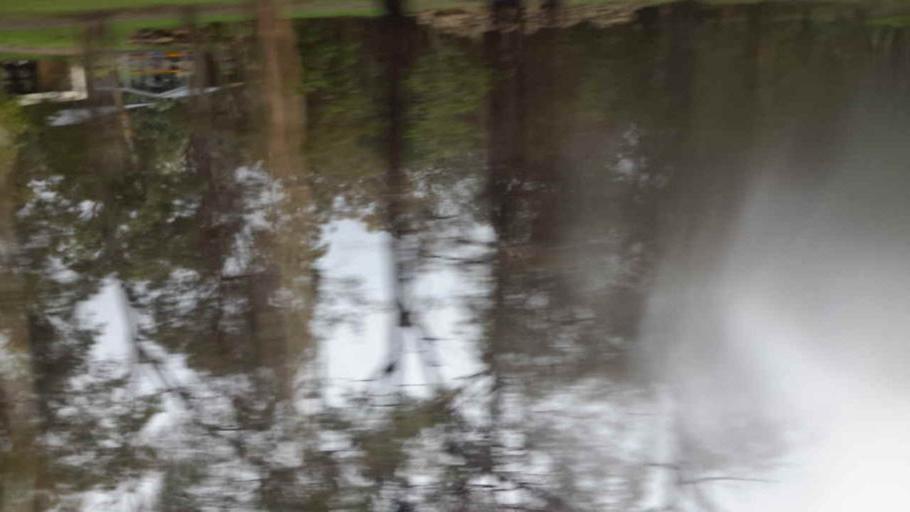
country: AU
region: New South Wales
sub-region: Wollondilly
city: Douglas Park
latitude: -34.2091
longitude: 150.7198
